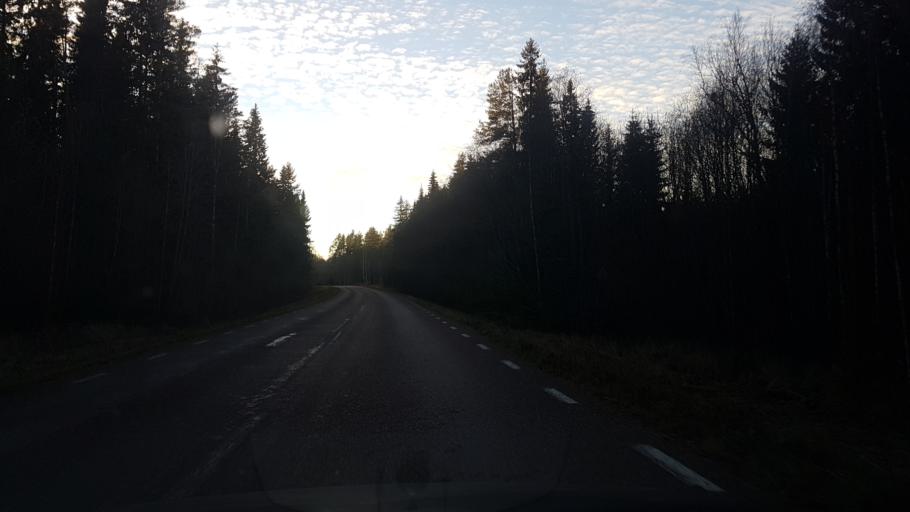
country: SE
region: Dalarna
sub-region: Leksand Municipality
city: Smedby
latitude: 60.7451
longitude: 15.2093
